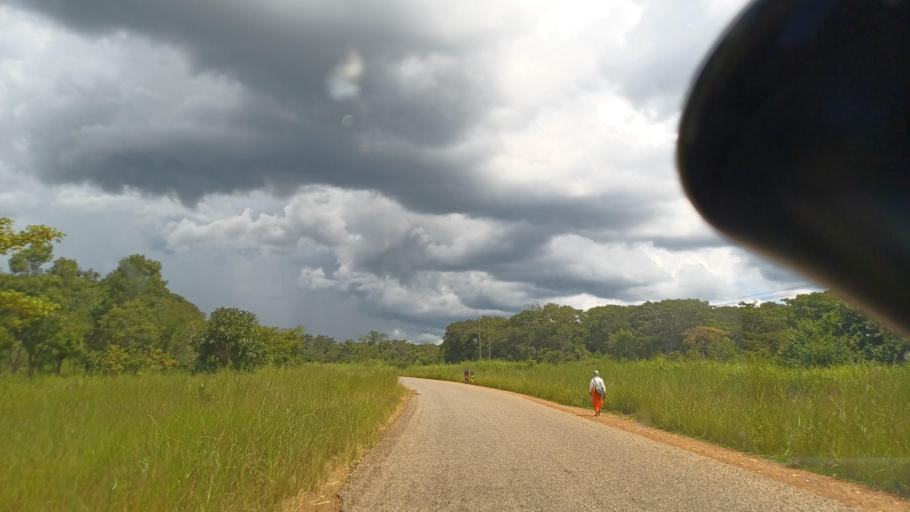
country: ZM
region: North-Western
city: Kasempa
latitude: -12.7790
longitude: 26.0093
